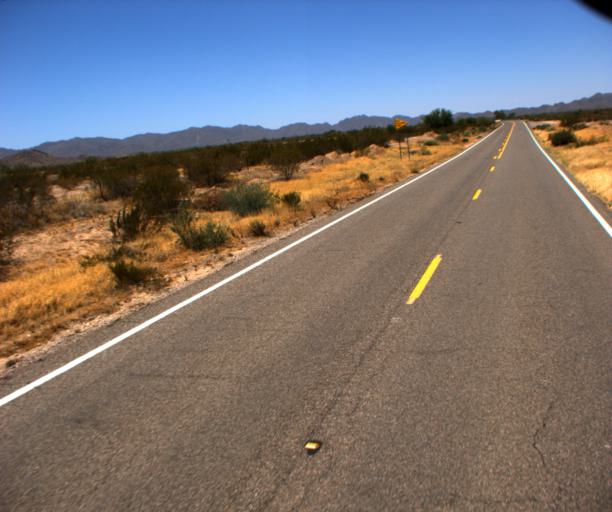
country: US
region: Arizona
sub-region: Pinal County
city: Maricopa
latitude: 33.0318
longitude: -112.3612
